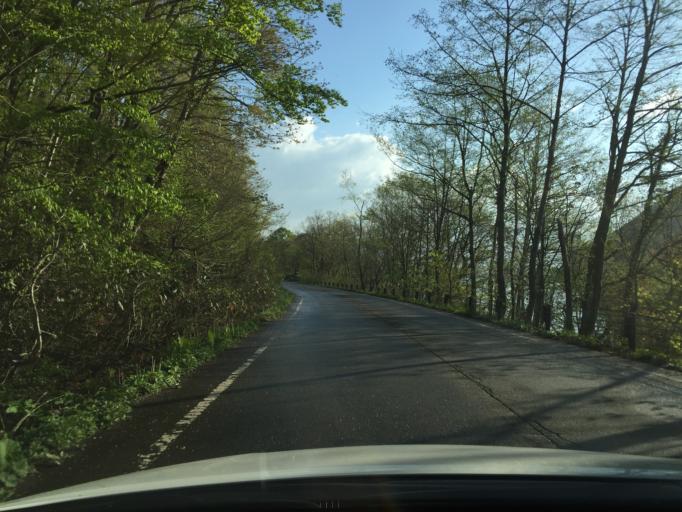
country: JP
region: Fukushima
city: Inawashiro
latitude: 37.6494
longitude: 140.0375
